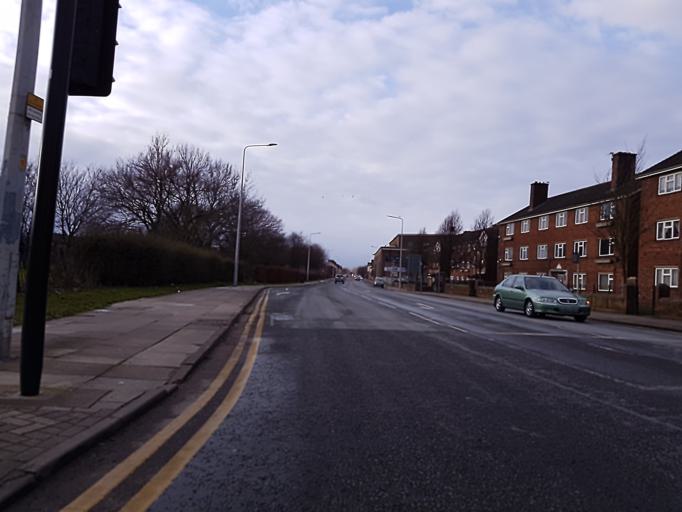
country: GB
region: England
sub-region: North East Lincolnshire
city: Grimsby
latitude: 53.5740
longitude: -0.0652
